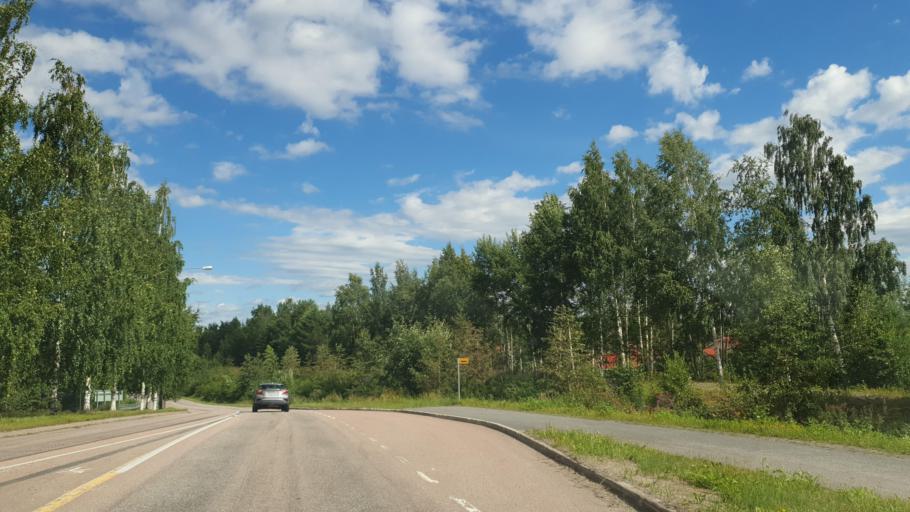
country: FI
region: Central Finland
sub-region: Jyvaeskylae
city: Saeynaetsalo
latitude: 62.1373
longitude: 25.7352
